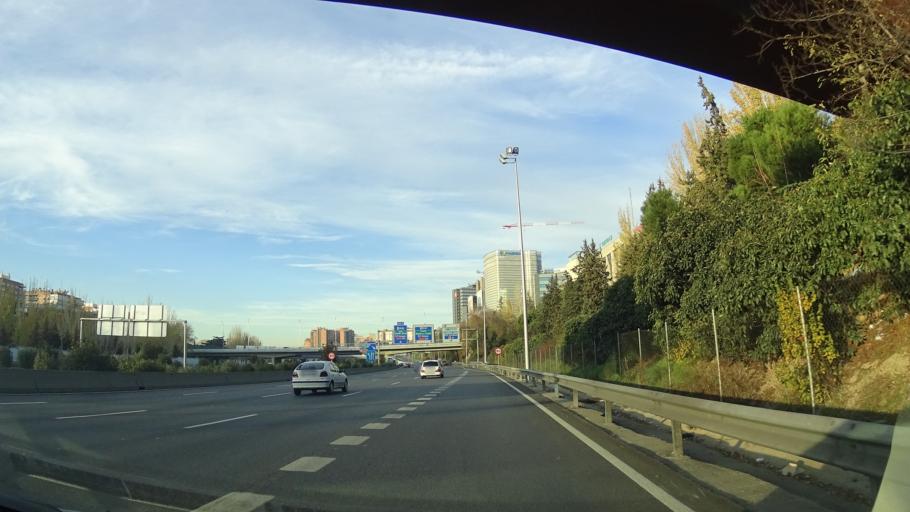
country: ES
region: Madrid
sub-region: Provincia de Madrid
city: Ciudad Lineal
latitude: 40.4388
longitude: -3.6588
